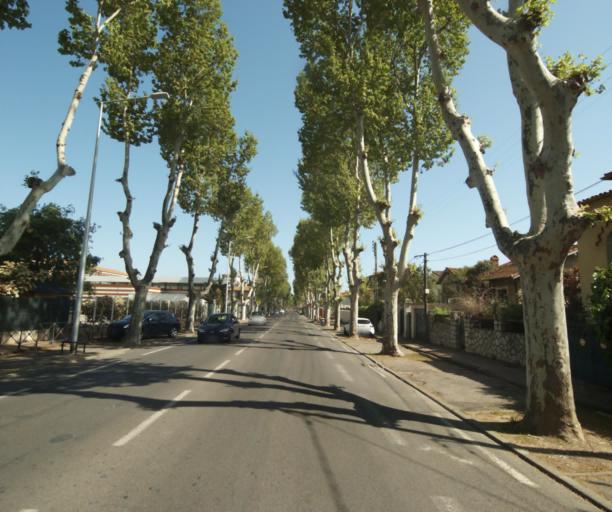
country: FR
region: Languedoc-Roussillon
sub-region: Departement de l'Herault
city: Montpellier
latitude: 43.6168
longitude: 3.8615
